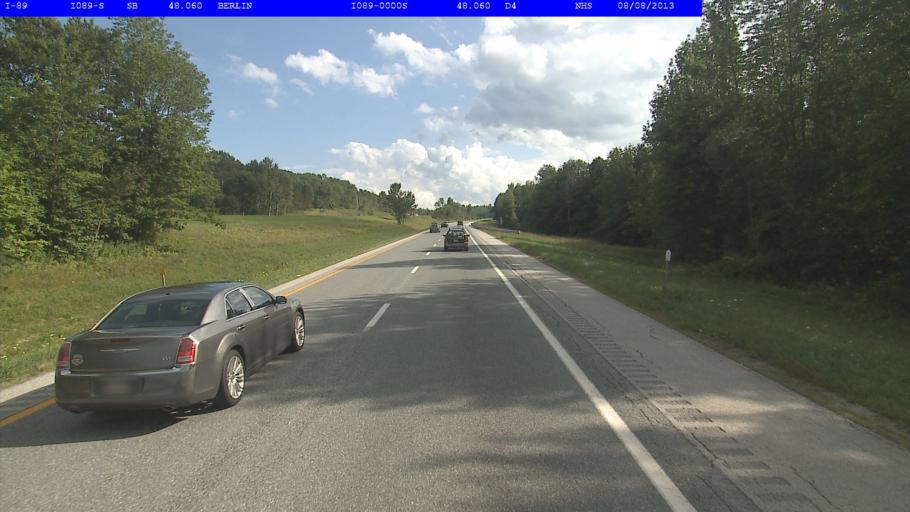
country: US
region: Vermont
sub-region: Washington County
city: South Barre
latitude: 44.1842
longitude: -72.5764
